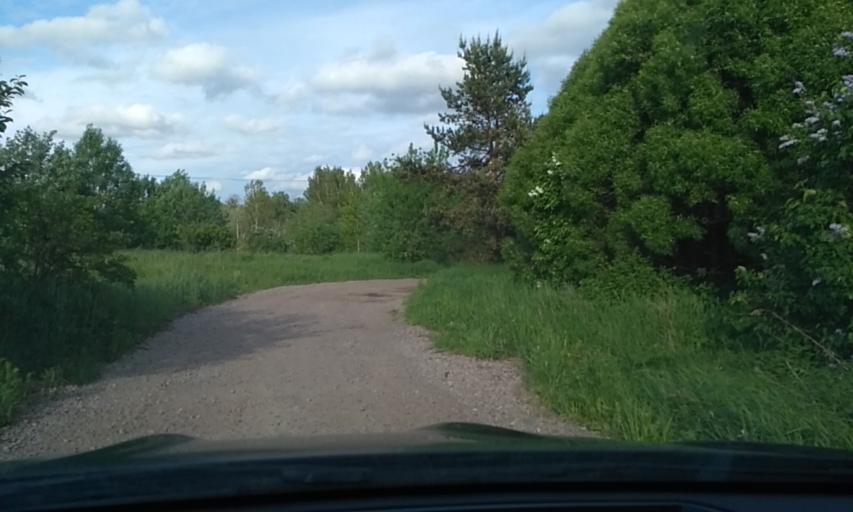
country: RU
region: Leningrad
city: Otradnoye
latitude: 59.8066
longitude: 30.8256
